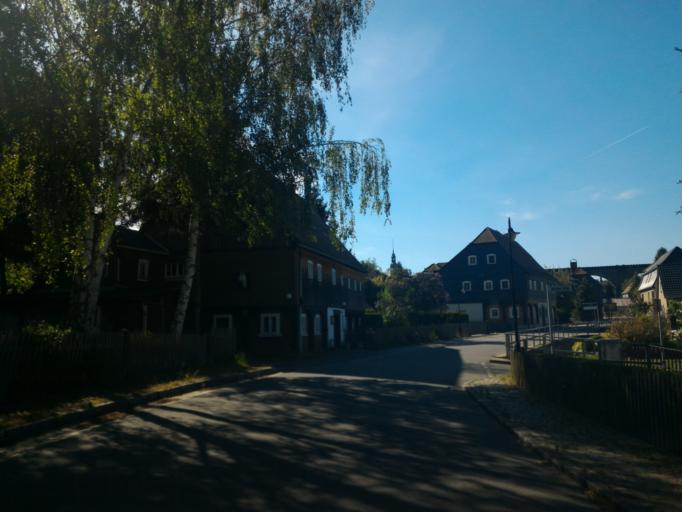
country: DE
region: Saxony
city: Niedercunnersdorf
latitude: 51.0389
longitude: 14.6662
